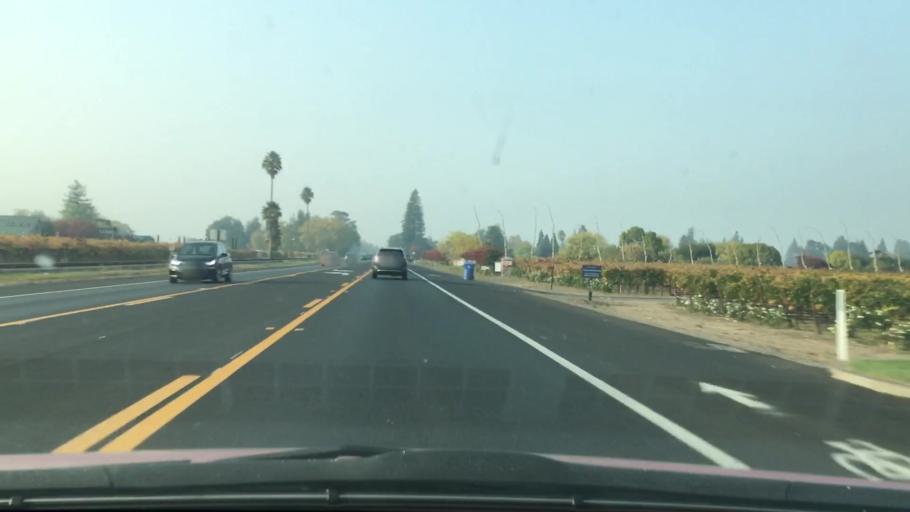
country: US
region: California
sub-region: Napa County
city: Saint Helena
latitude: 38.4534
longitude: -122.4176
